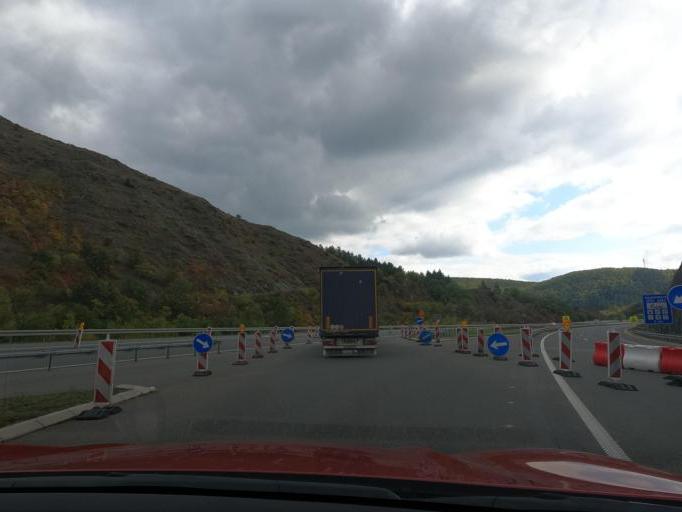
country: RS
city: Prislonica
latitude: 43.9866
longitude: 20.4021
